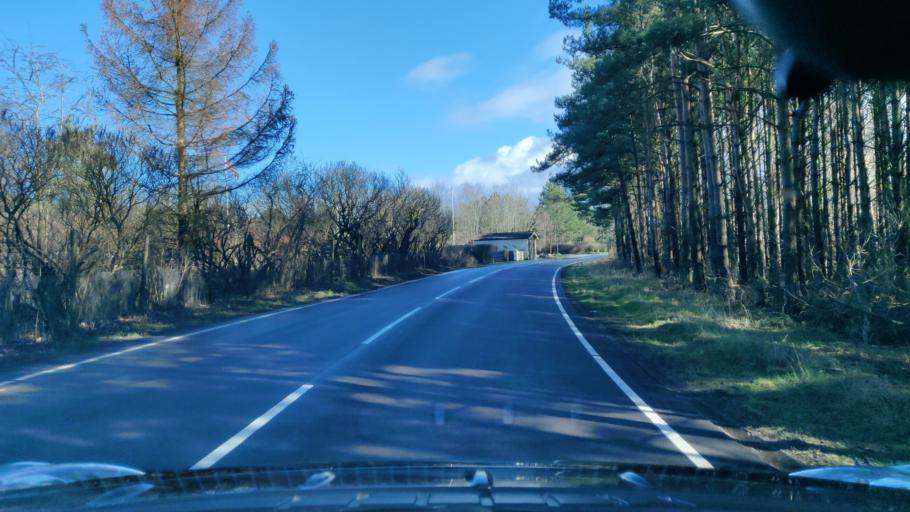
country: DK
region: Zealand
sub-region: Odsherred Kommune
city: Hojby
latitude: 55.8917
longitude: 11.5617
